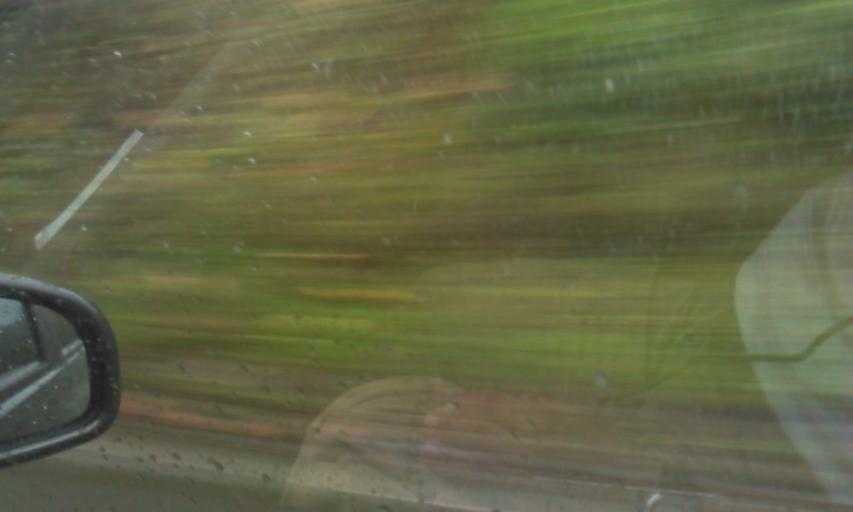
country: CO
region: Valle del Cauca
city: Buenaventura
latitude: 3.8665
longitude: -76.8280
